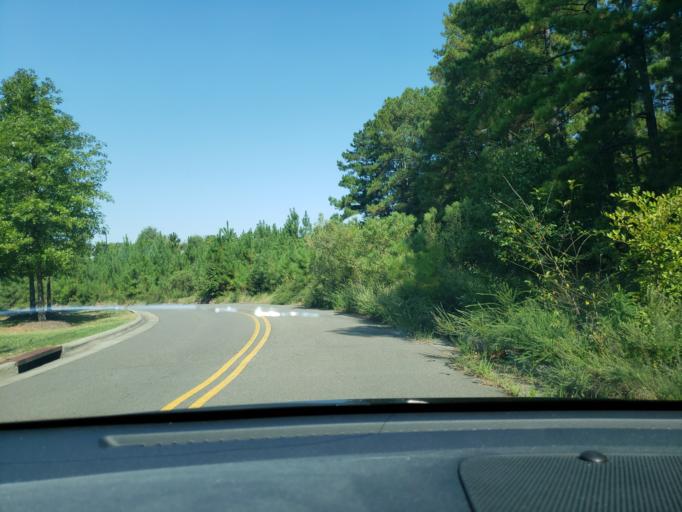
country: US
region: North Carolina
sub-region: Durham County
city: Durham
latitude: 35.9013
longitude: -78.8868
